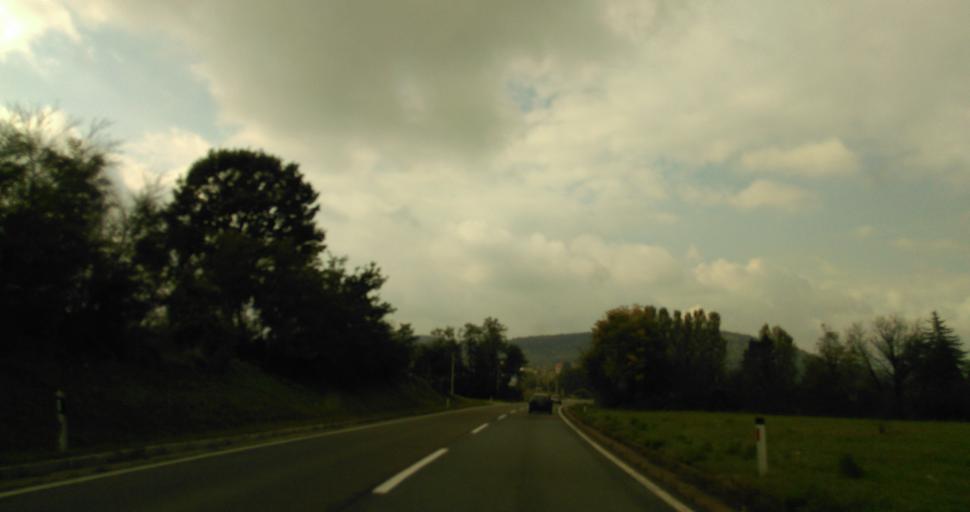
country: RS
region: Central Serbia
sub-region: Kolubarski Okrug
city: Ljig
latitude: 44.2470
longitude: 20.2828
